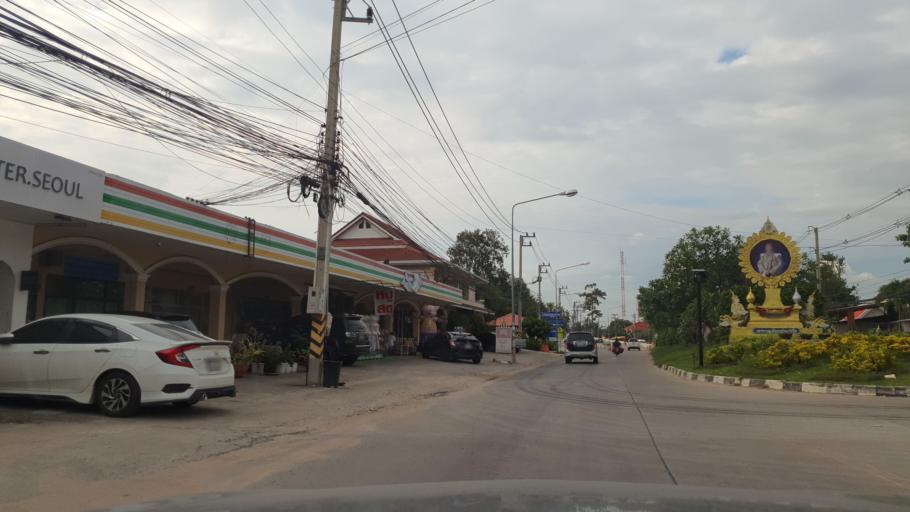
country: TH
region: Chon Buri
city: Phatthaya
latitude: 12.9461
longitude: 100.9373
